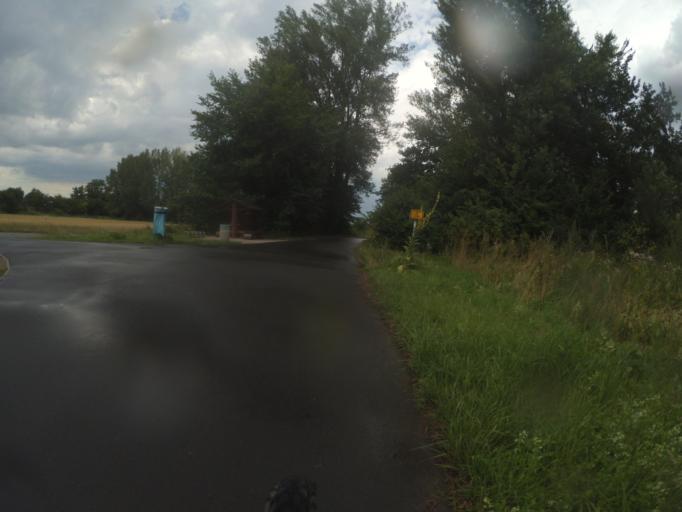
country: CZ
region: Central Bohemia
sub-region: Okres Melnik
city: Melnik
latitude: 50.3614
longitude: 14.4560
